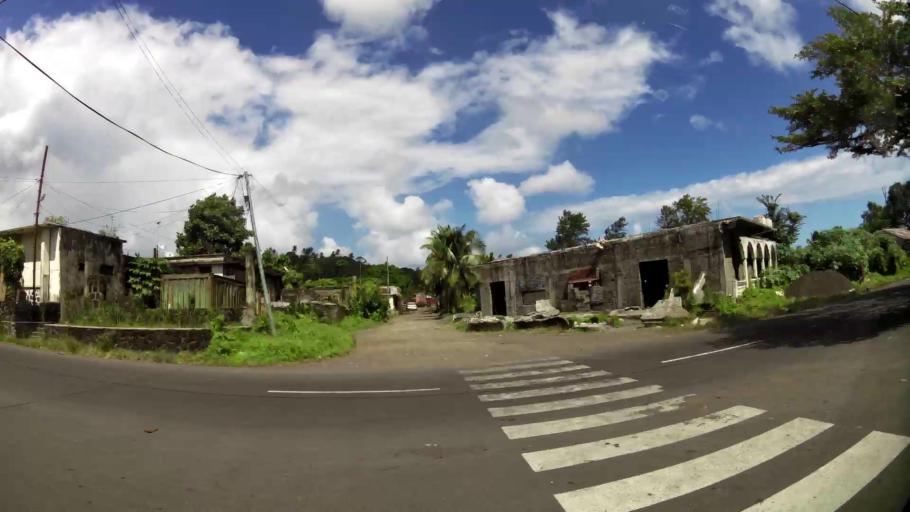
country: KM
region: Grande Comore
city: Mavingouni
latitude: -11.7198
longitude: 43.2487
